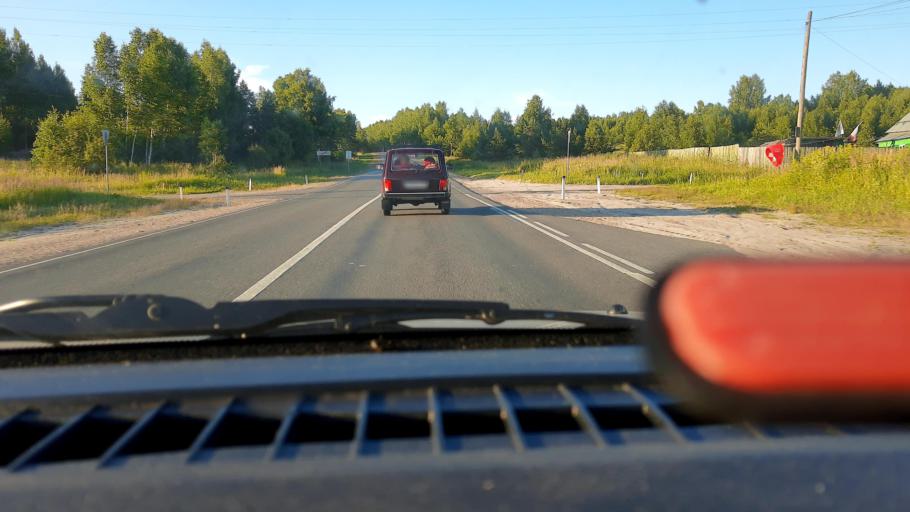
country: RU
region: Nizjnij Novgorod
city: Krasnyye Baki
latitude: 57.0438
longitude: 45.1314
